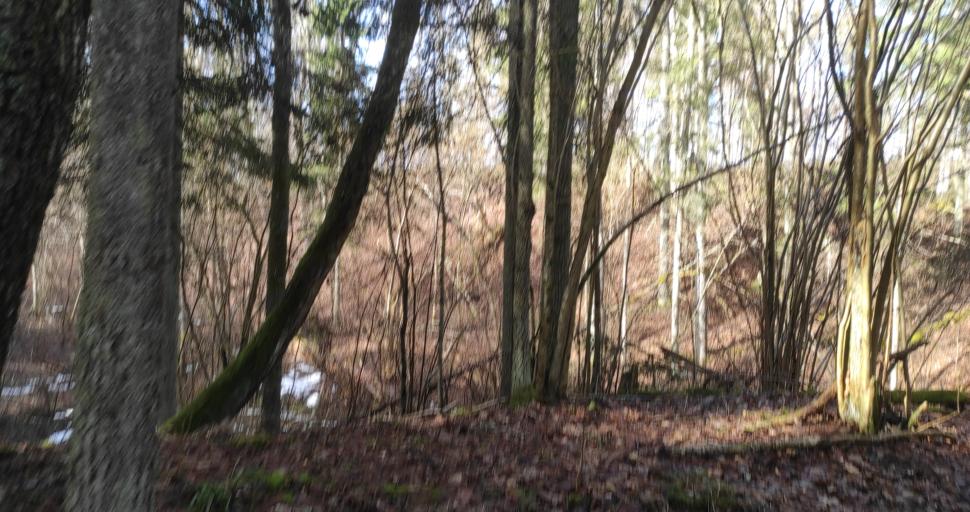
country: LV
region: Tukuma Rajons
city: Tukums
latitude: 57.1136
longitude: 23.0369
